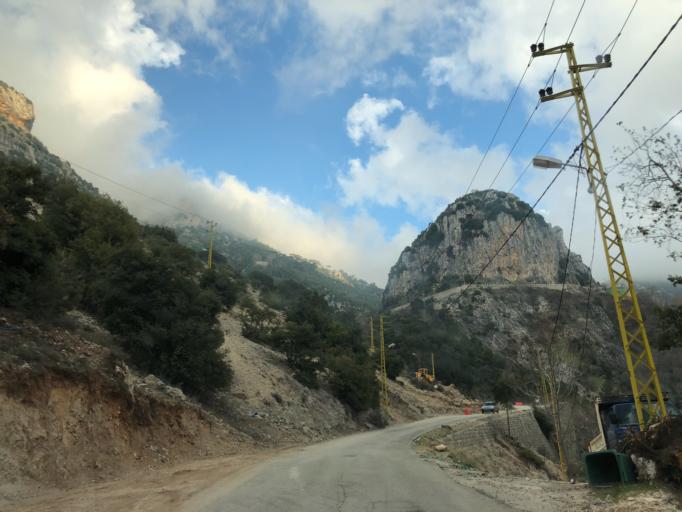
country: LB
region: Liban-Nord
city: Amioun
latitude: 34.1966
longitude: 35.8884
